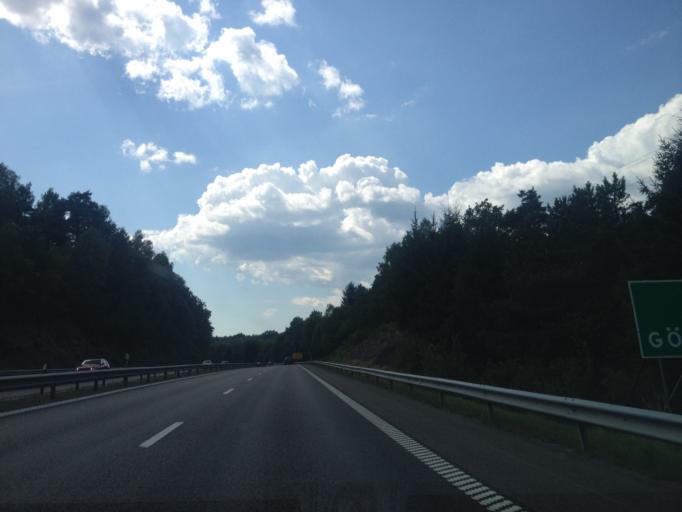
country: SE
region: Vaestra Goetaland
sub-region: Lerums Kommun
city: Lerum
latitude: 57.7481
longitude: 12.2326
